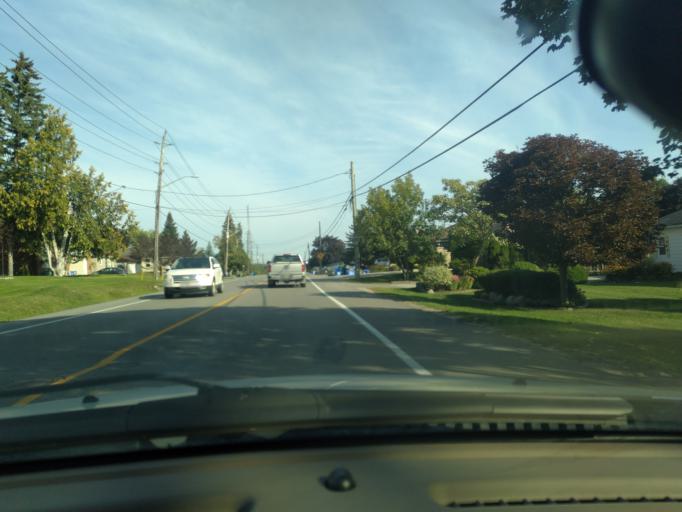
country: CA
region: Ontario
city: Barrie
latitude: 44.3666
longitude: -79.6690
